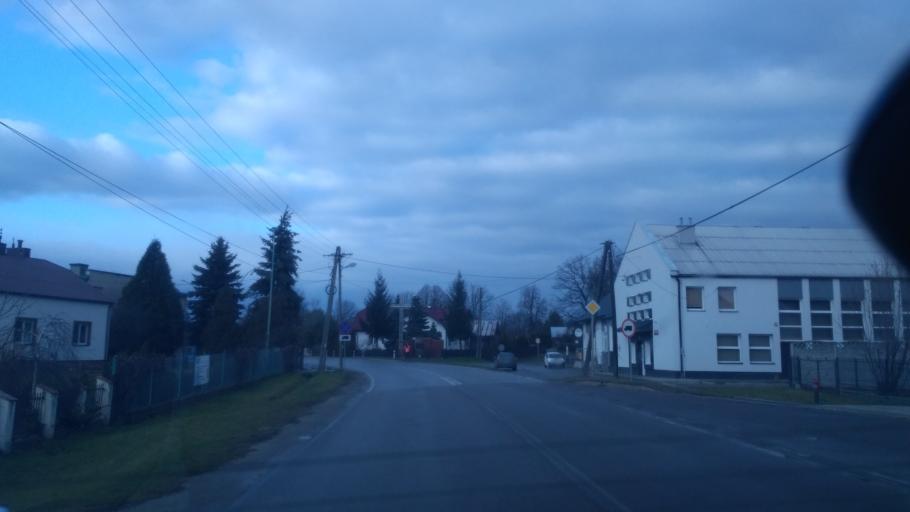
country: PL
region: Subcarpathian Voivodeship
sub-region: Powiat lancucki
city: Czarna
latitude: 50.1110
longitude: 22.1808
